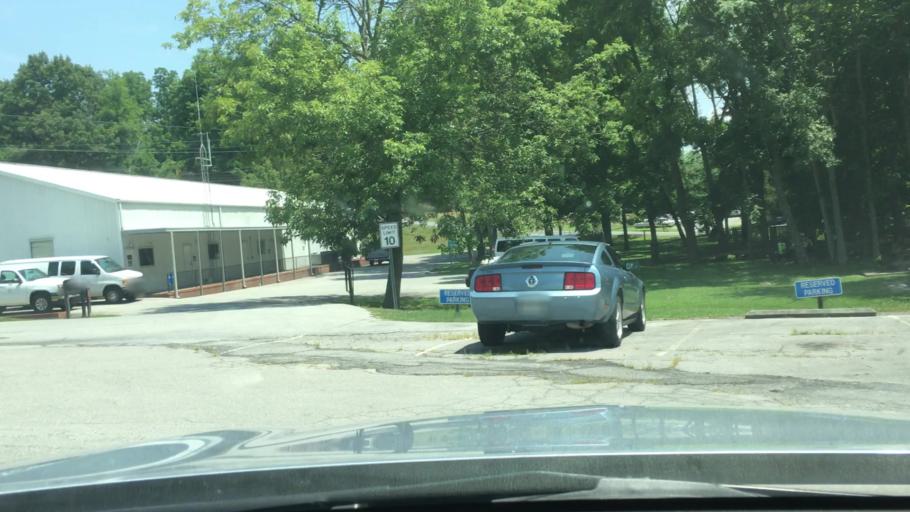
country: US
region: Tennessee
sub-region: Sullivan County
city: Blountville
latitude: 36.5341
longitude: -82.3268
